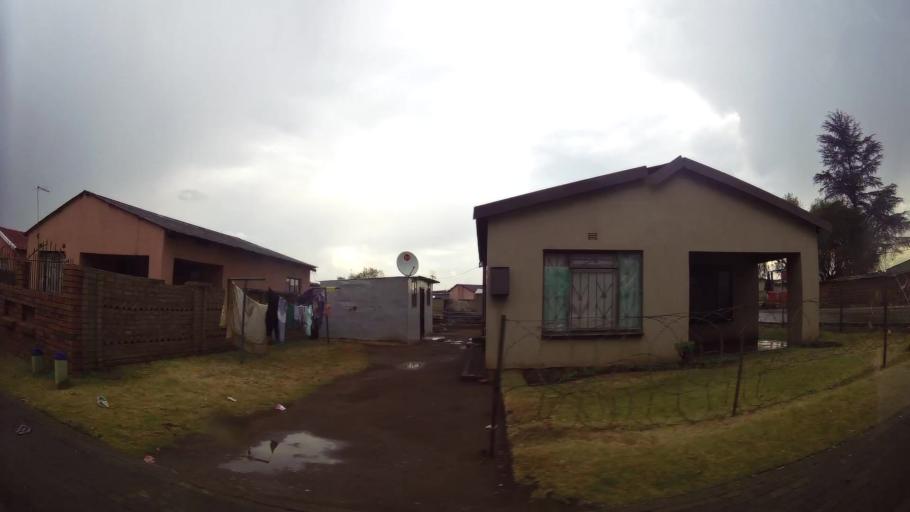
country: ZA
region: Gauteng
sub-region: Ekurhuleni Metropolitan Municipality
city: Germiston
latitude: -26.3646
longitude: 28.1412
